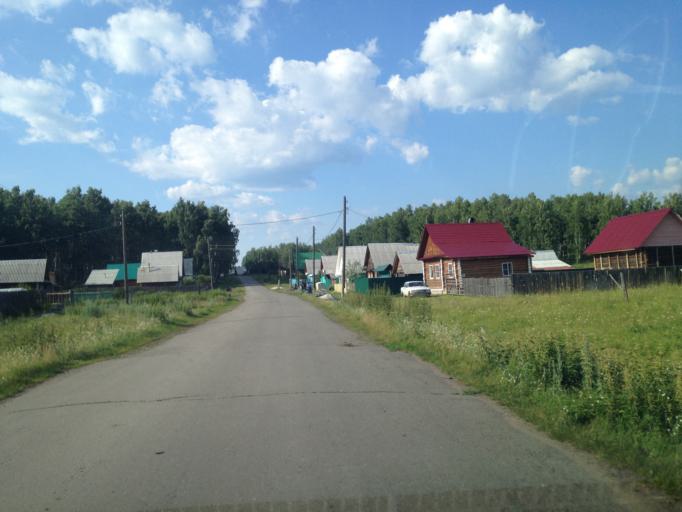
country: RU
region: Chelyabinsk
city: Snezhinsk
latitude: 56.1702
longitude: 60.5660
